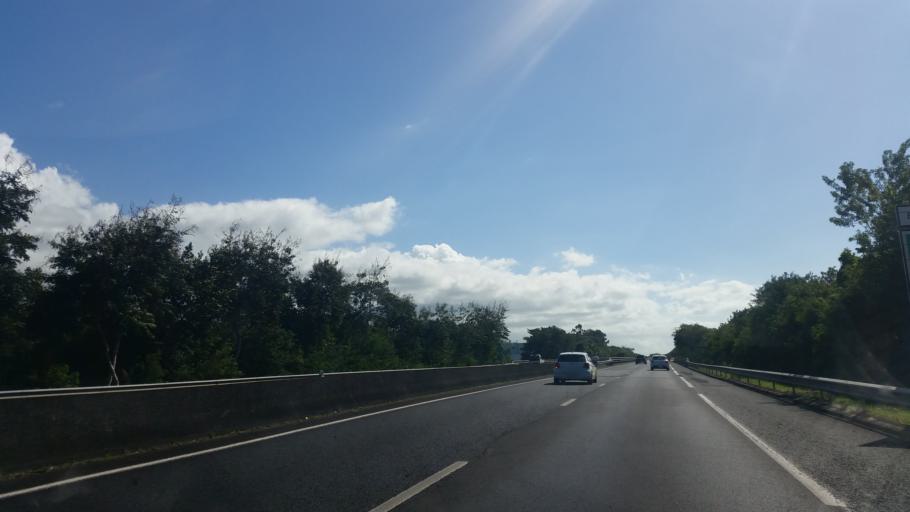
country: RE
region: Reunion
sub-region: Reunion
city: Bras-Panon
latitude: -21.0046
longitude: 55.6789
